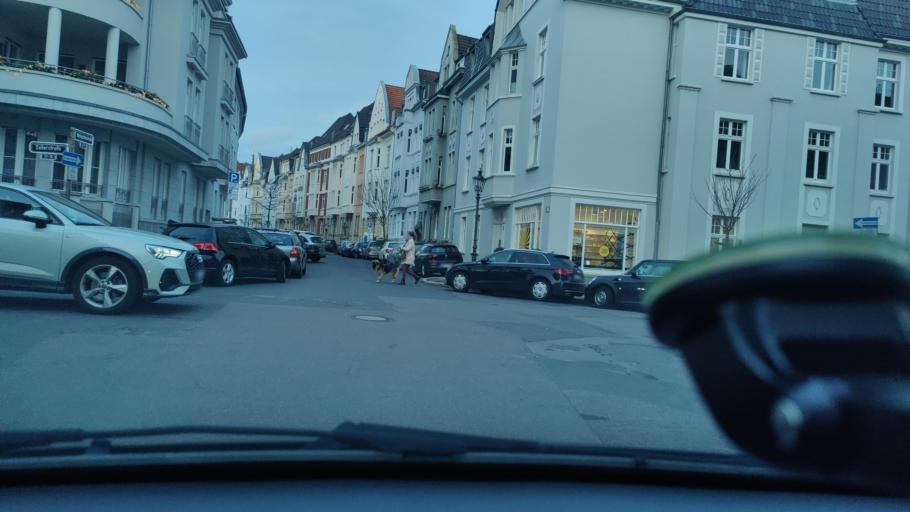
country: DE
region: North Rhine-Westphalia
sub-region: Regierungsbezirk Dusseldorf
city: Dusseldorf
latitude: 51.2296
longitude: 6.7600
